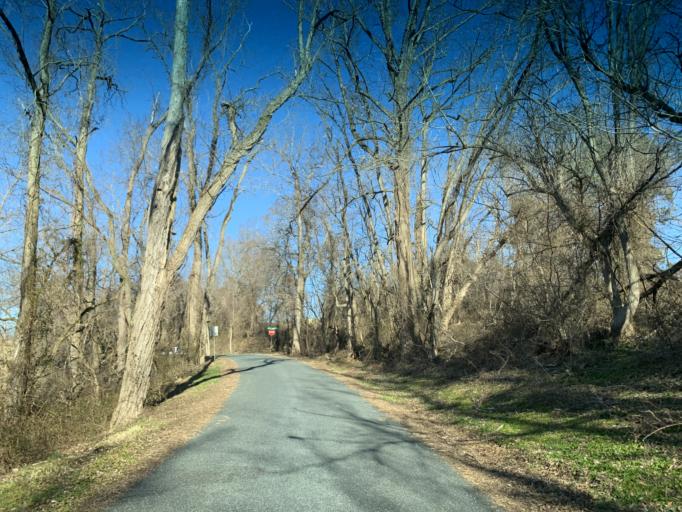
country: US
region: Maryland
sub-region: Harford County
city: South Bel Air
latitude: 39.6214
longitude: -76.2492
